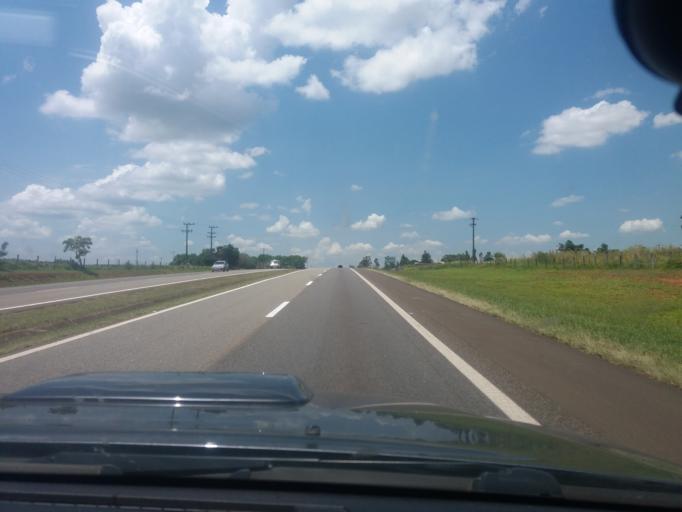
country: BR
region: Sao Paulo
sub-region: Itapetininga
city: Itapetininga
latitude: -23.5755
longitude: -47.9796
